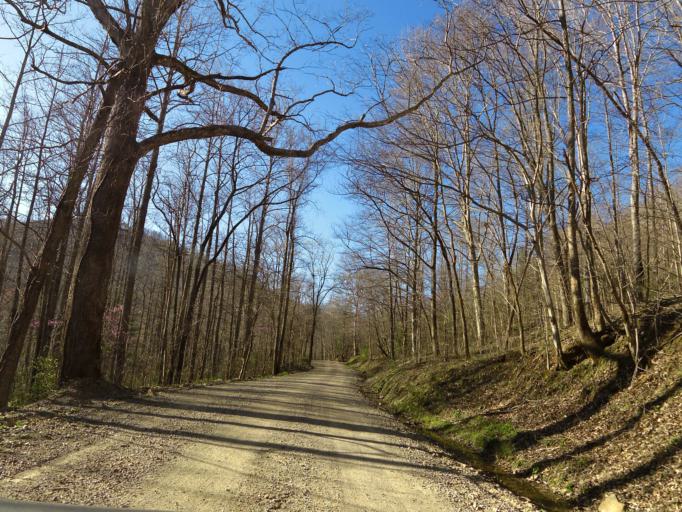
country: US
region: Tennessee
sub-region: Roane County
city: Oliver Springs
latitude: 36.2262
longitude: -84.4156
